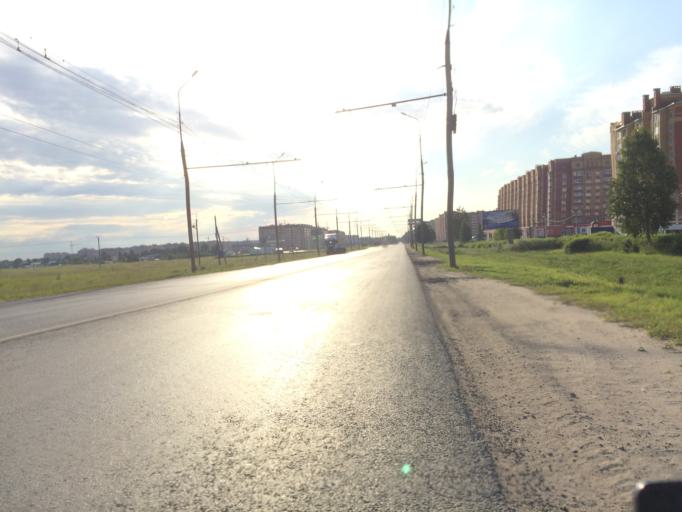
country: RU
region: Mariy-El
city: Medvedevo
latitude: 56.6393
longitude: 47.8085
